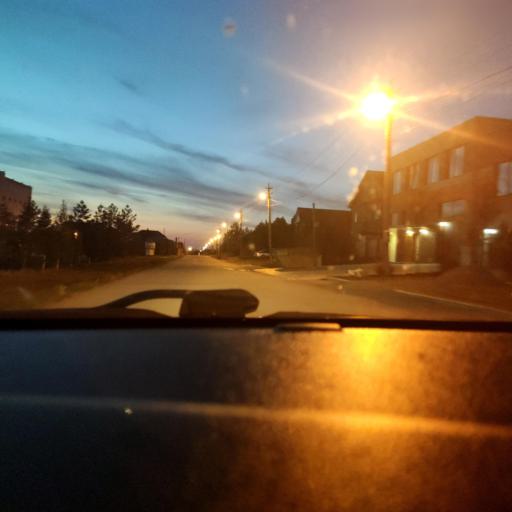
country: RU
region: Bashkortostan
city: Ufa
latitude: 54.5977
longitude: 55.9401
